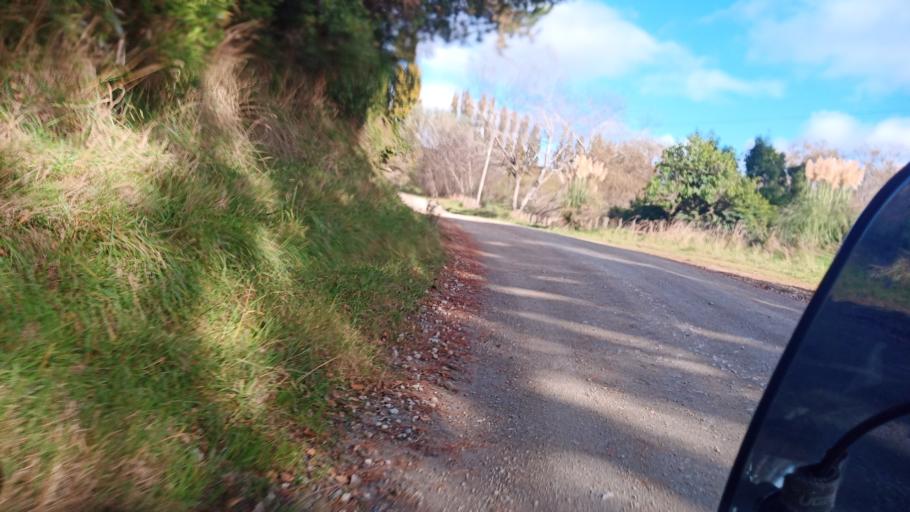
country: NZ
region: Gisborne
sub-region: Gisborne District
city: Gisborne
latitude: -38.5363
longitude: 177.5231
